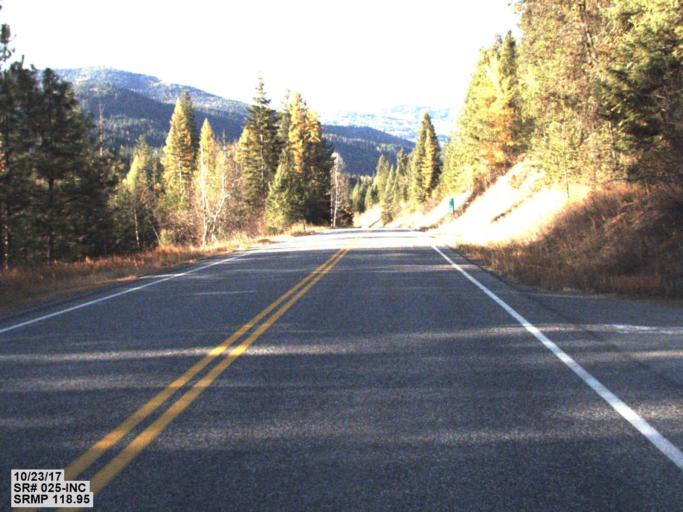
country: CA
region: British Columbia
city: Rossland
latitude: 48.9711
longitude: -117.8139
